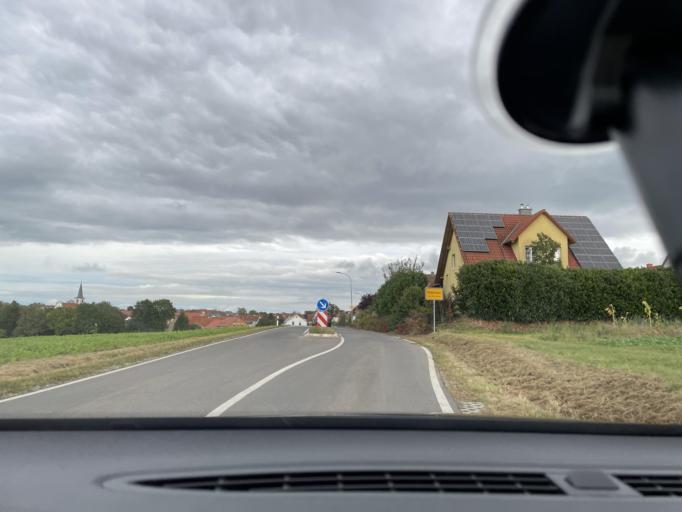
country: DE
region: Bavaria
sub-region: Regierungsbezirk Unterfranken
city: Rodelmaier
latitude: 50.3195
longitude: 10.2703
